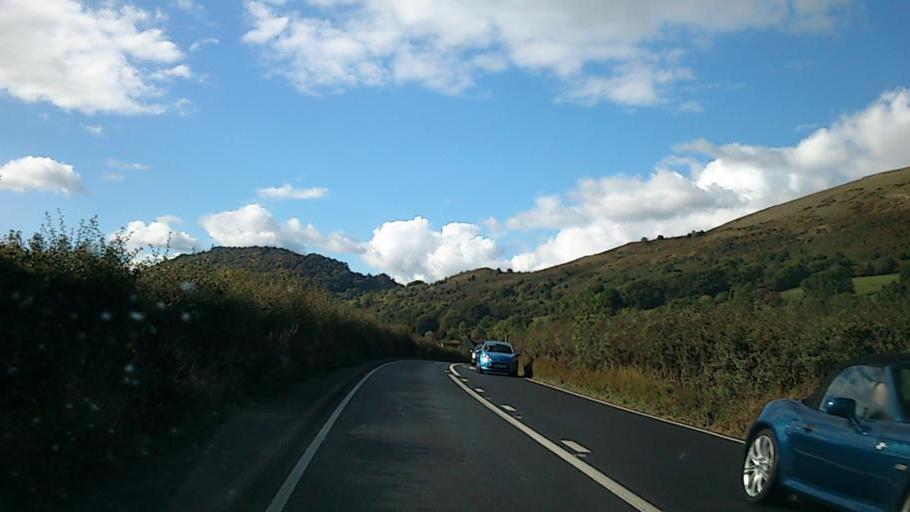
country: GB
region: England
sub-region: Shropshire
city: Westbury
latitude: 52.7076
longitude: -3.0170
